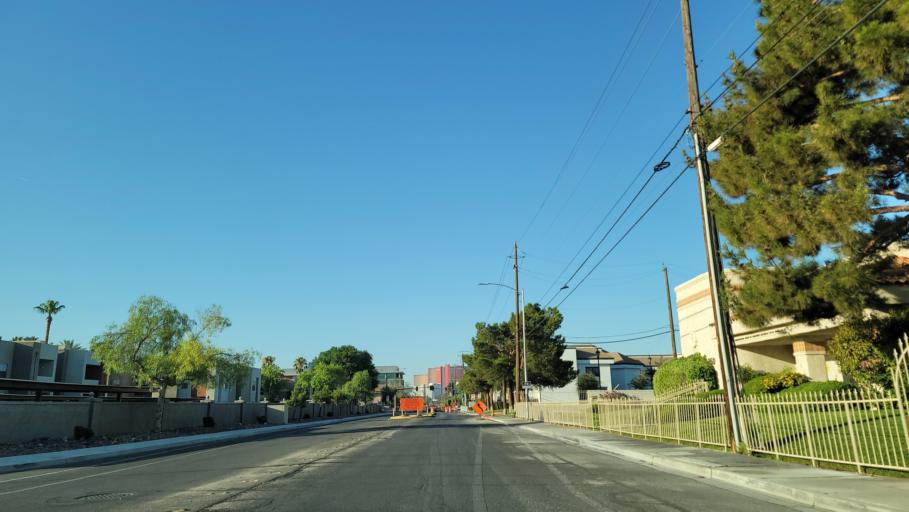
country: US
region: Nevada
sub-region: Clark County
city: Las Vegas
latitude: 36.1681
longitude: -115.1655
